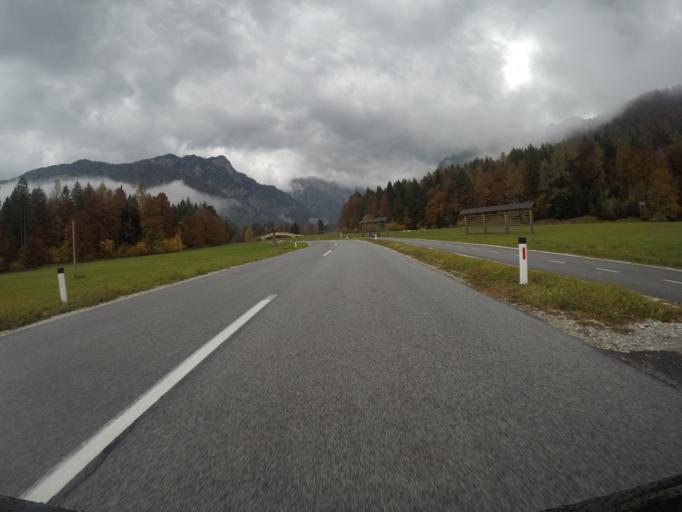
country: AT
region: Carinthia
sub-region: Politischer Bezirk Villach Land
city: Arnoldstein
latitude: 46.4889
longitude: 13.7239
